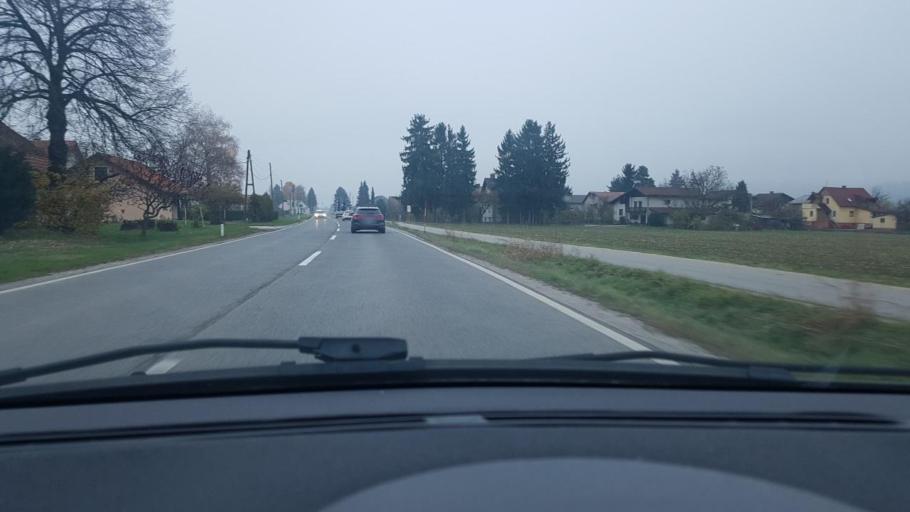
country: SI
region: Zalec
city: Zalec
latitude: 46.2457
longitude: 15.1973
